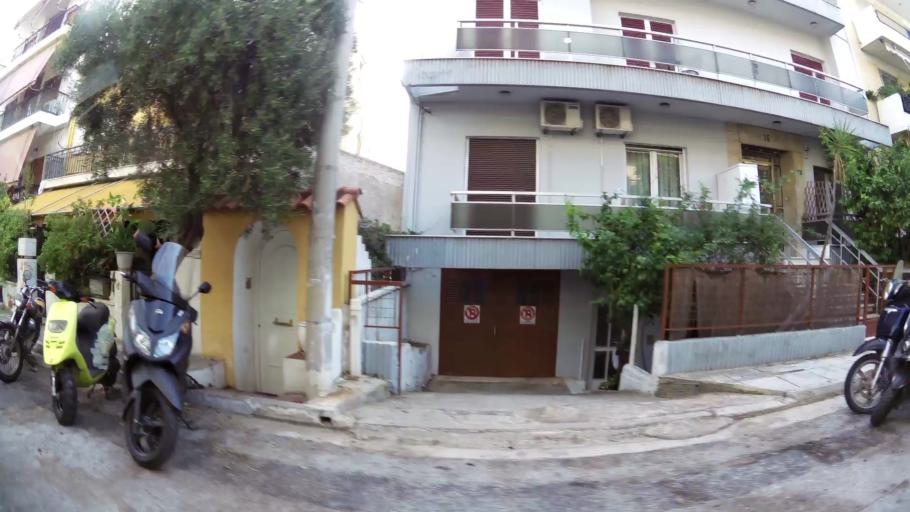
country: GR
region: Attica
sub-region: Nomarchia Athinas
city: Psychiko
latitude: 37.9985
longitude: 23.7600
